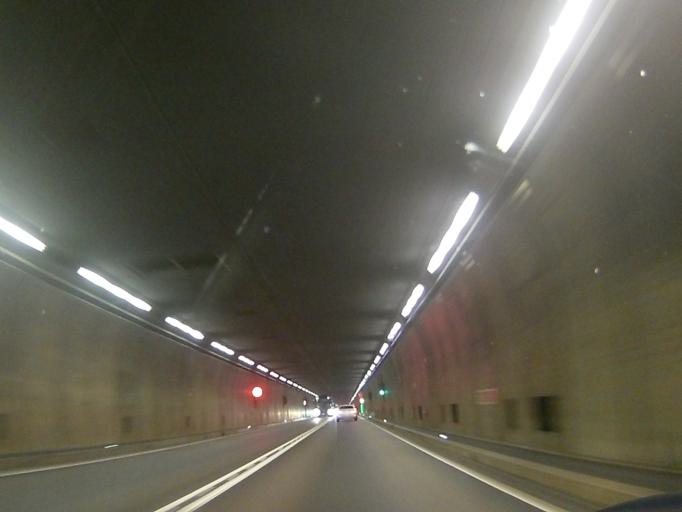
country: CH
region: Uri
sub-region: Uri
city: Andermatt
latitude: 46.6362
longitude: 8.5771
